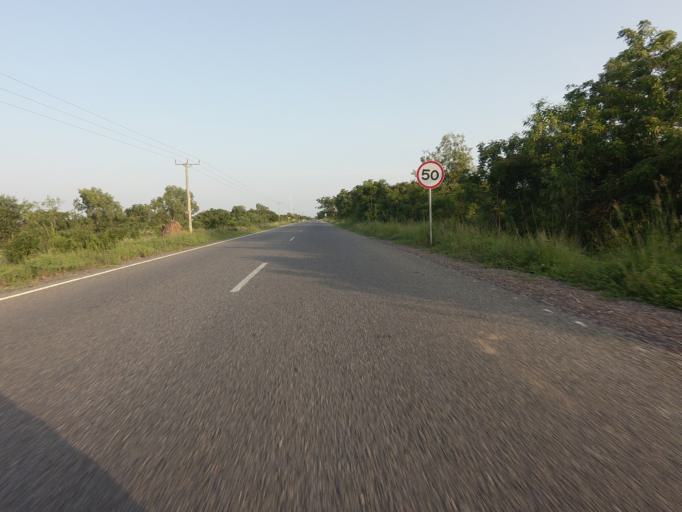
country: GH
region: Volta
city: Anloga
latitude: 5.9107
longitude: 0.7094
